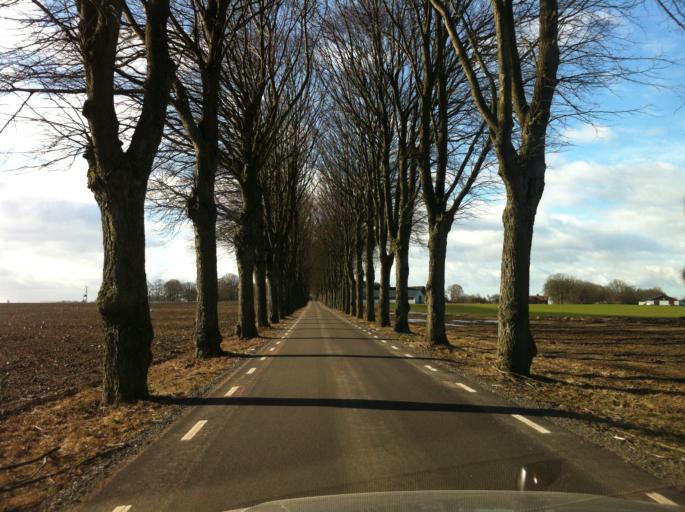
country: SE
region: Skane
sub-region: Landskrona
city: Asmundtorp
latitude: 55.9445
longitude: 13.0055
